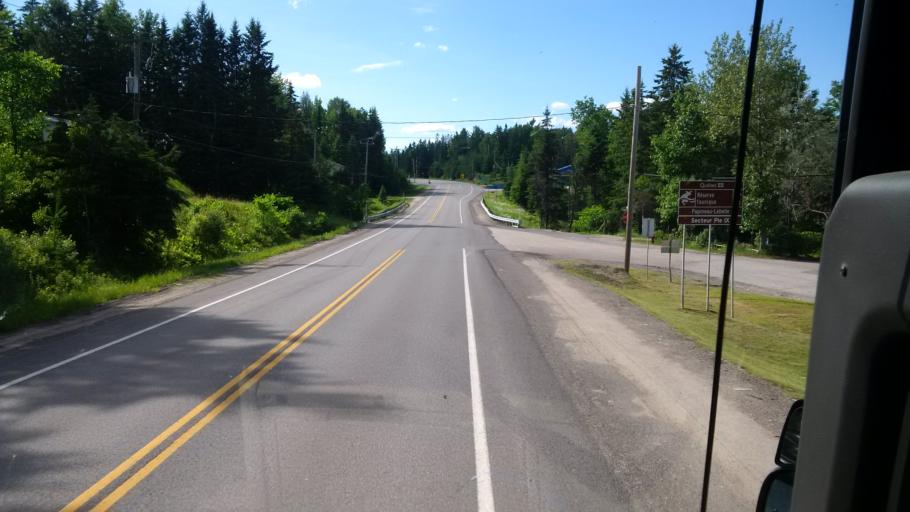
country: CA
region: Quebec
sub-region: Laurentides
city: Riviere-Rouge
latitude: 46.4329
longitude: -74.8969
